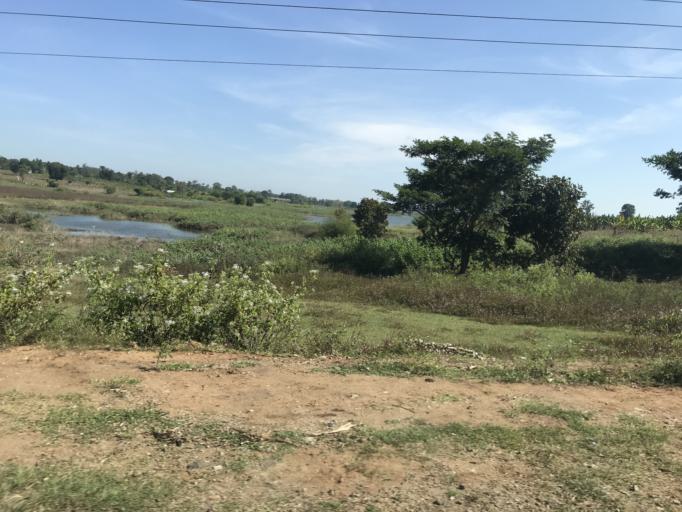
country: IN
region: Karnataka
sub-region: Mysore
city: Heggadadevankote
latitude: 11.9660
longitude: 76.2562
